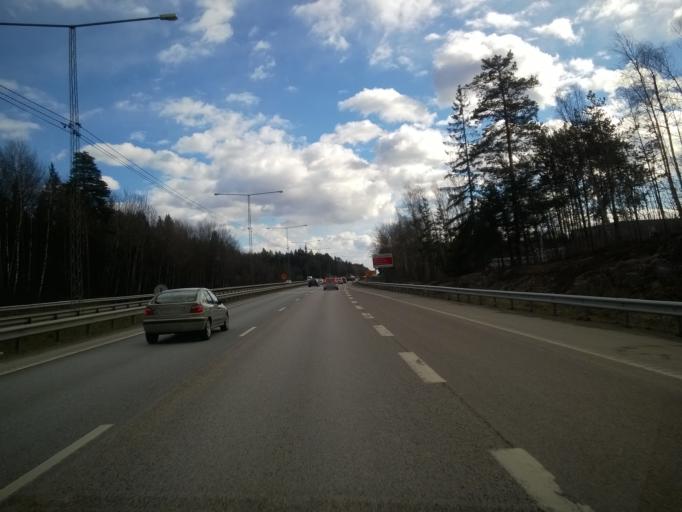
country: SE
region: Stockholm
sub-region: Jarfalla Kommun
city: Jakobsberg
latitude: 59.4460
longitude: 17.8407
